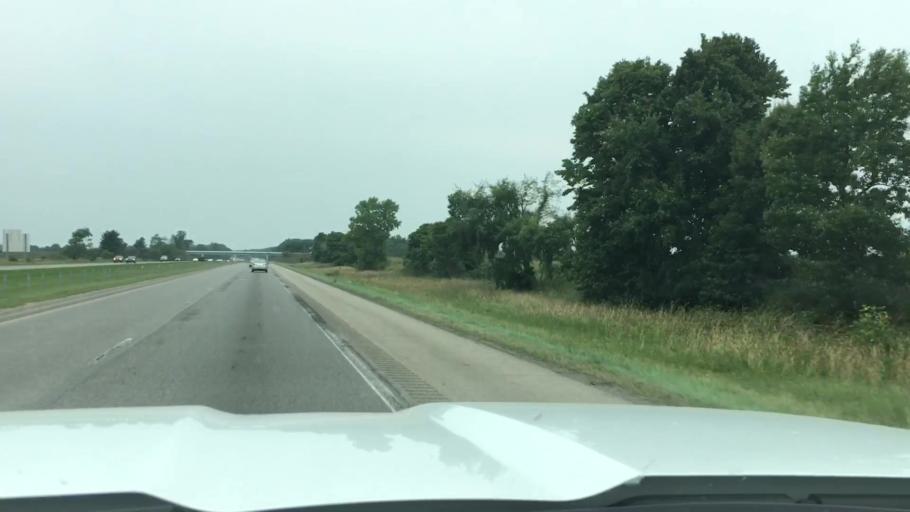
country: US
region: Michigan
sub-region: Ingham County
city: Webberville
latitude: 42.6652
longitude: -84.2207
